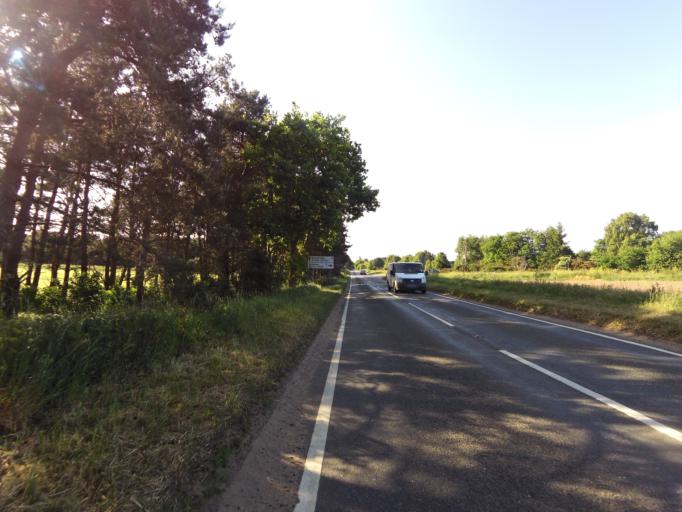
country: GB
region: England
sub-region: Suffolk
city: Woodbridge
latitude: 52.0914
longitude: 1.3531
